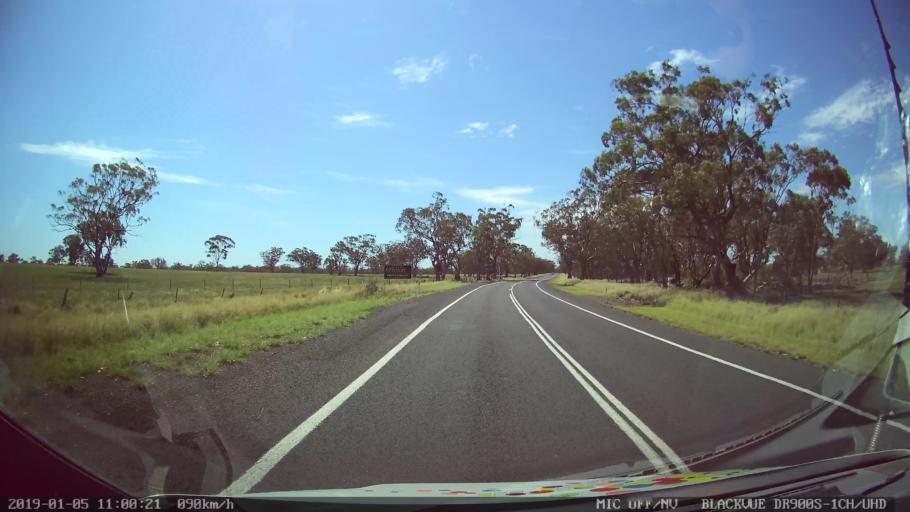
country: AU
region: New South Wales
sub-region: Warrumbungle Shire
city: Coonabarabran
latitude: -31.4168
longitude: 149.2105
